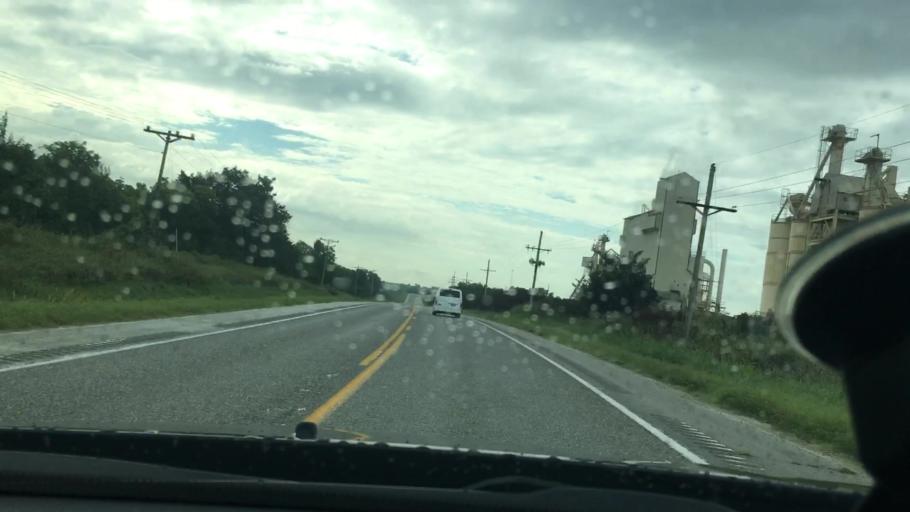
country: US
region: Oklahoma
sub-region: Johnston County
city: Tishomingo
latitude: 34.3412
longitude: -96.7953
